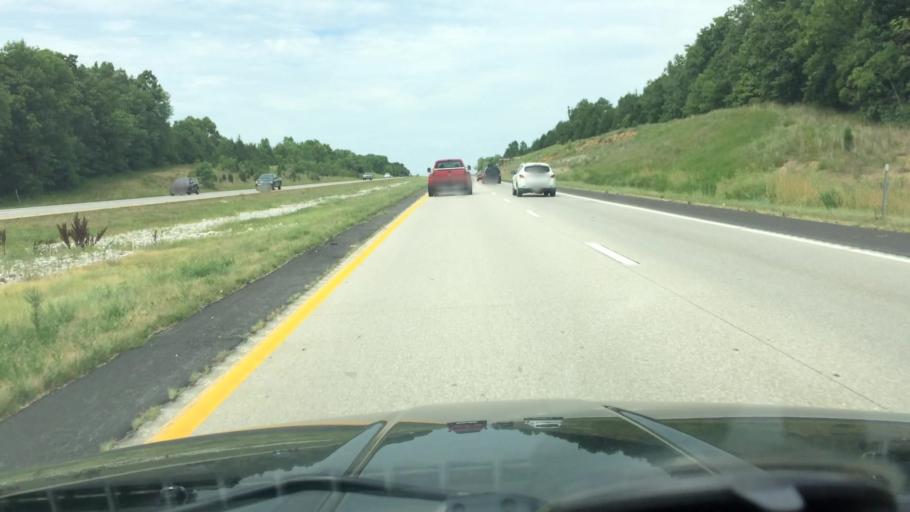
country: US
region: Missouri
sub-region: Greene County
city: Willard
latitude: 37.4382
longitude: -93.3555
